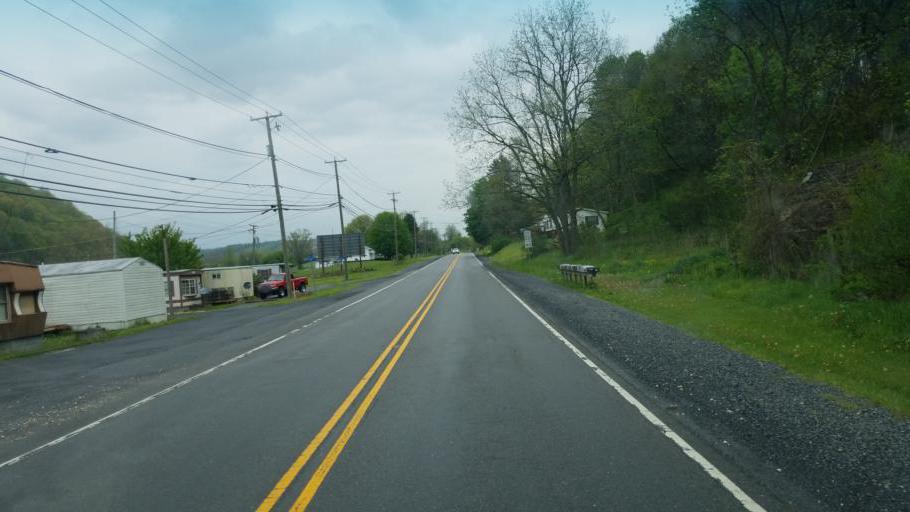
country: US
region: Virginia
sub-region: Smyth County
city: Atkins
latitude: 36.8582
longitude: -81.4606
